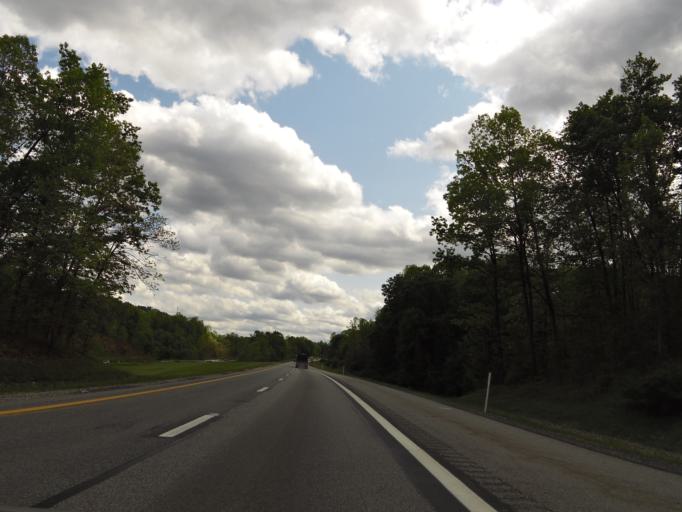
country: US
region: West Virginia
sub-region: Raleigh County
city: Bradley
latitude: 37.8987
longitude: -81.2680
